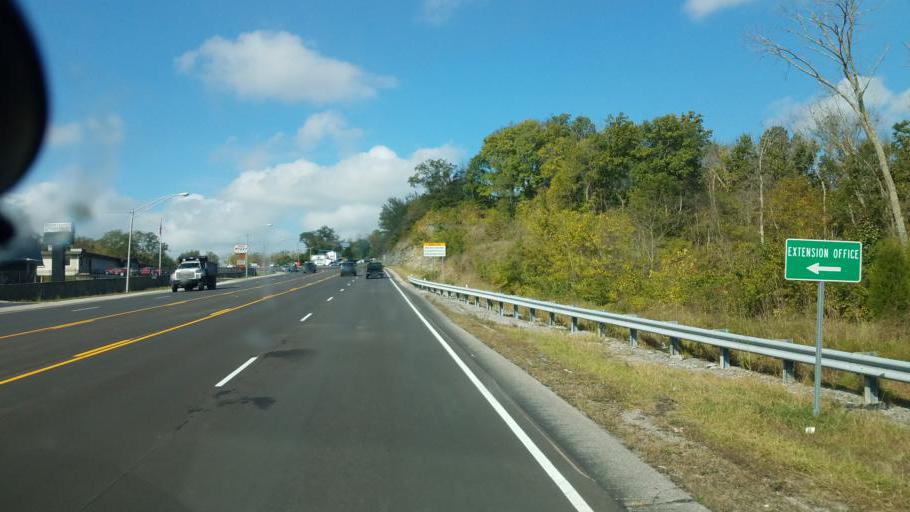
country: US
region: Ohio
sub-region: Brown County
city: Aberdeen
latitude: 38.6436
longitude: -83.7743
